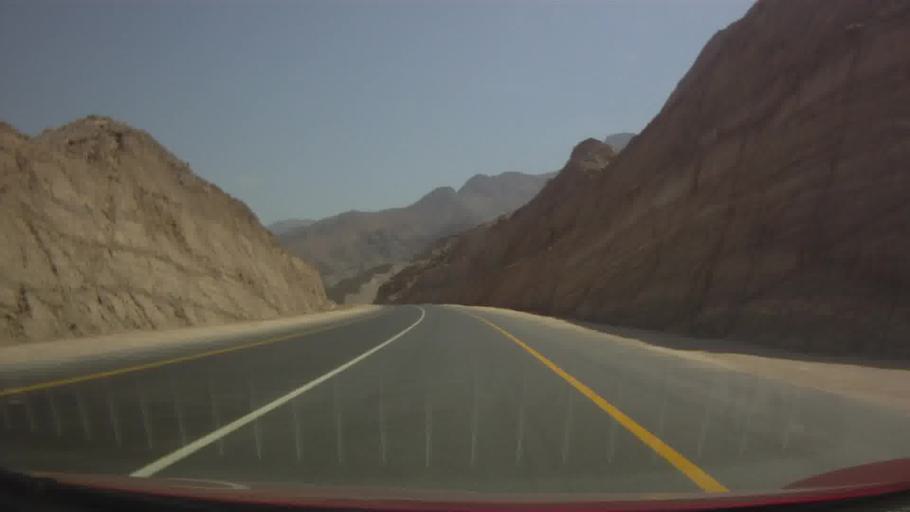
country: OM
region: Muhafazat Masqat
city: Muscat
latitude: 23.3993
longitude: 58.7822
